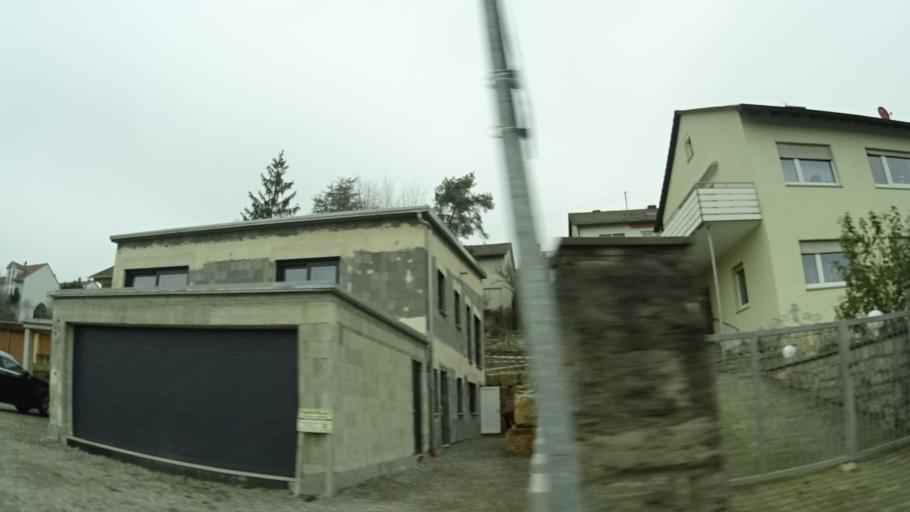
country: DE
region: Bavaria
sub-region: Regierungsbezirk Unterfranken
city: Ochsenfurt
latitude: 49.6688
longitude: 10.0683
